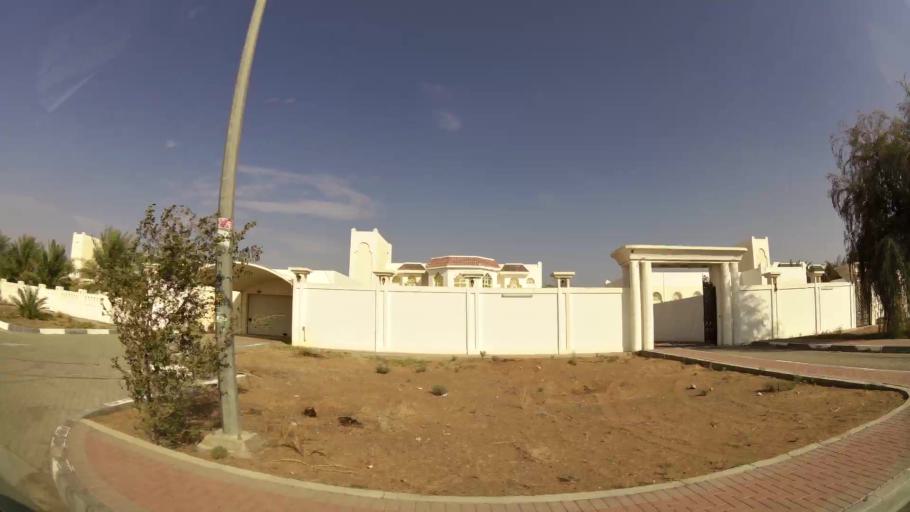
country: AE
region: Abu Dhabi
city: Al Ain
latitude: 24.0869
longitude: 55.8683
